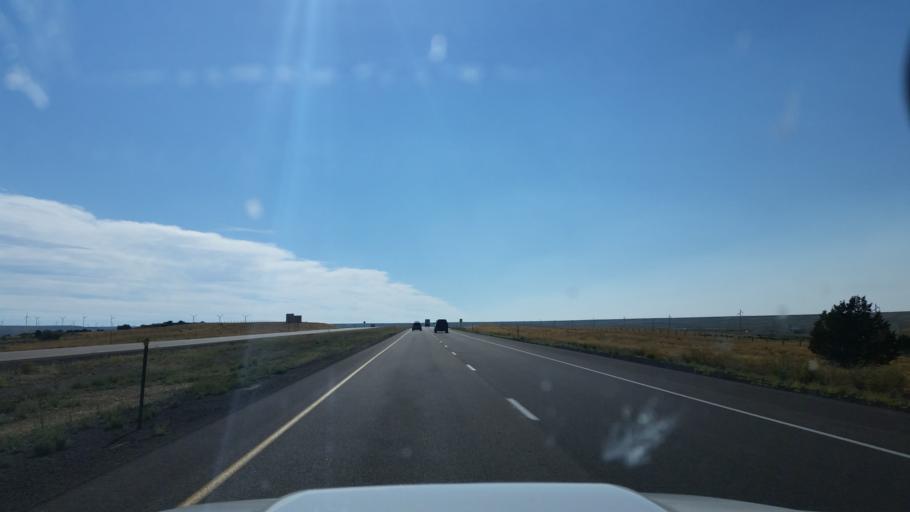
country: US
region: Wyoming
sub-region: Uinta County
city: Mountain View
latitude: 41.3289
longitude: -110.4502
